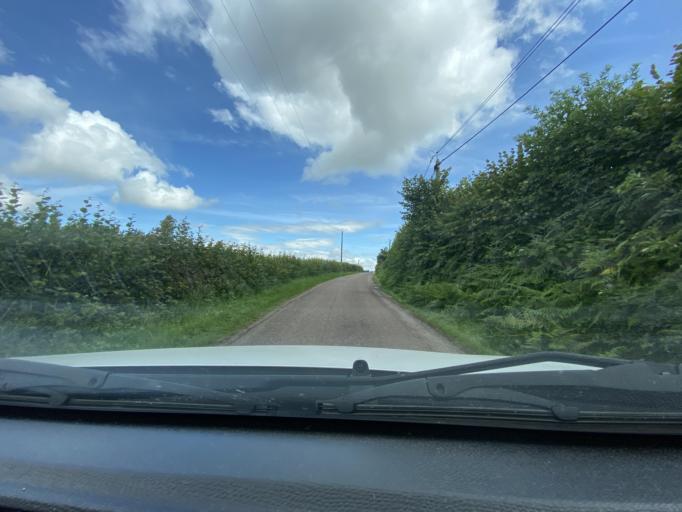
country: FR
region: Bourgogne
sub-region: Departement de la Cote-d'Or
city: Saulieu
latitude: 47.2633
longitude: 4.1905
